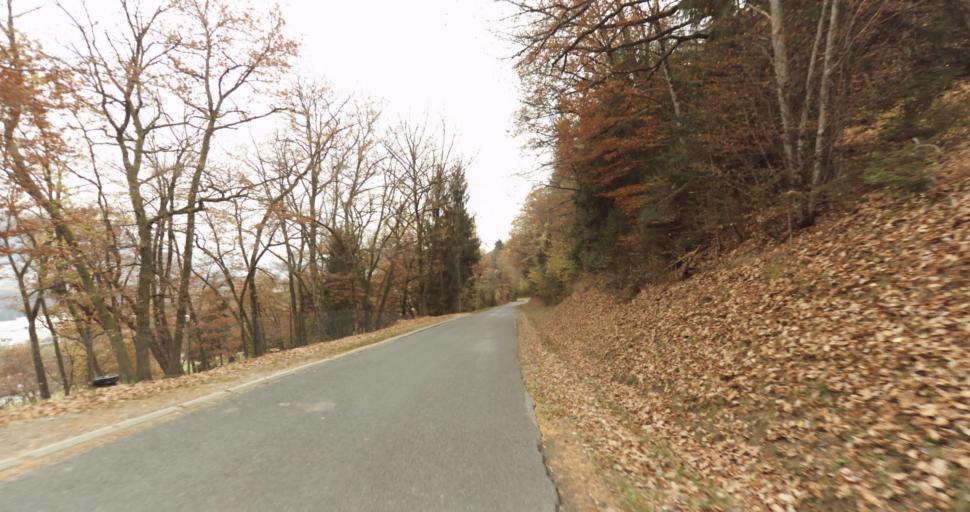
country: FR
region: Rhone-Alpes
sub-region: Departement de la Haute-Savoie
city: Saint-Martin-Bellevue
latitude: 45.9551
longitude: 6.1559
